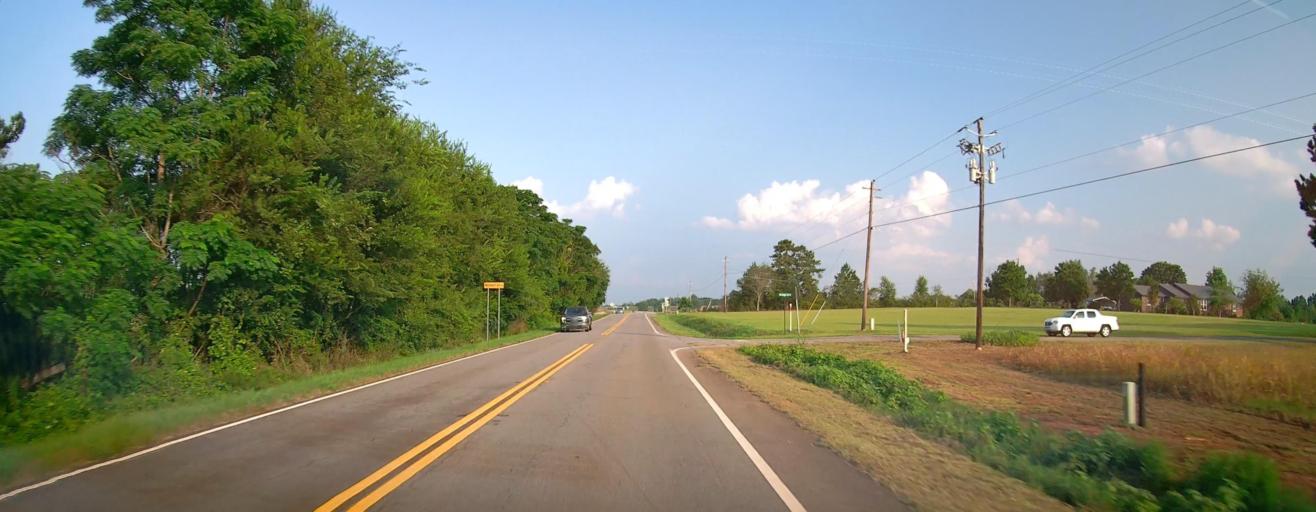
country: US
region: Georgia
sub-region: Jones County
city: Gray
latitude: 33.0359
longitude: -83.5424
